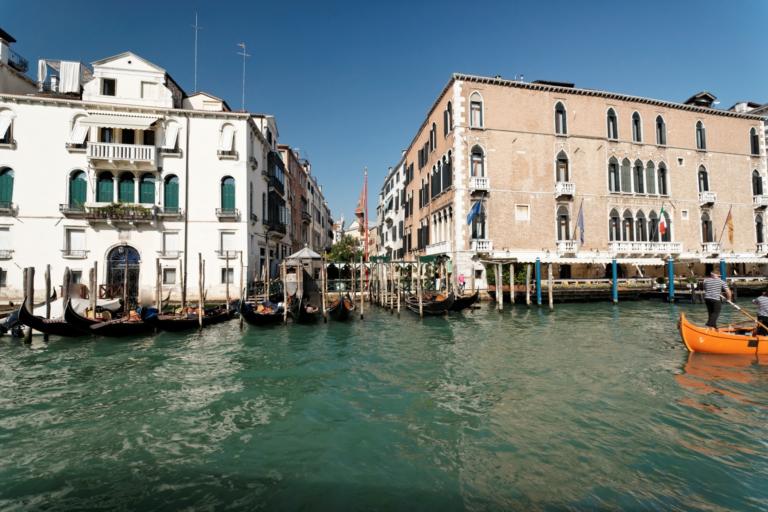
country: IT
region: Veneto
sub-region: Provincia di Venezia
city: Venice
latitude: 45.4314
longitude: 12.3330
